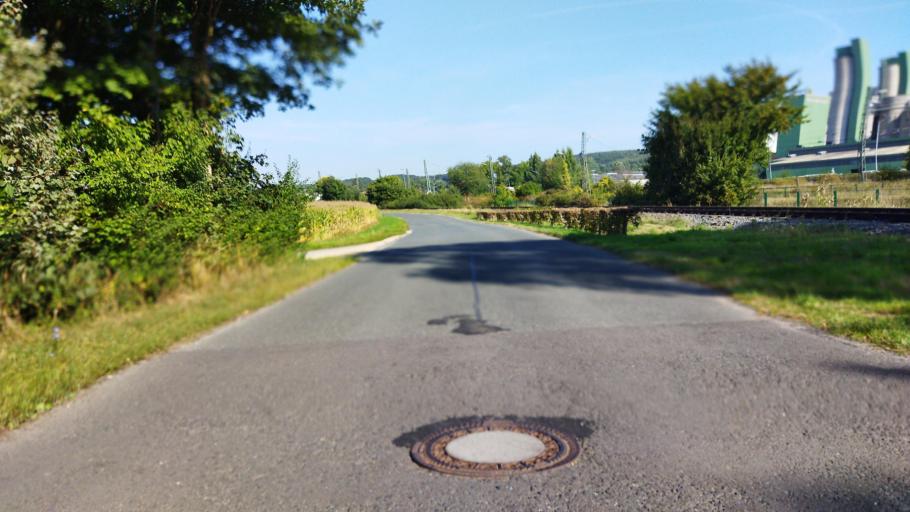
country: DE
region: North Rhine-Westphalia
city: Lengerich
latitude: 52.1706
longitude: 7.8849
